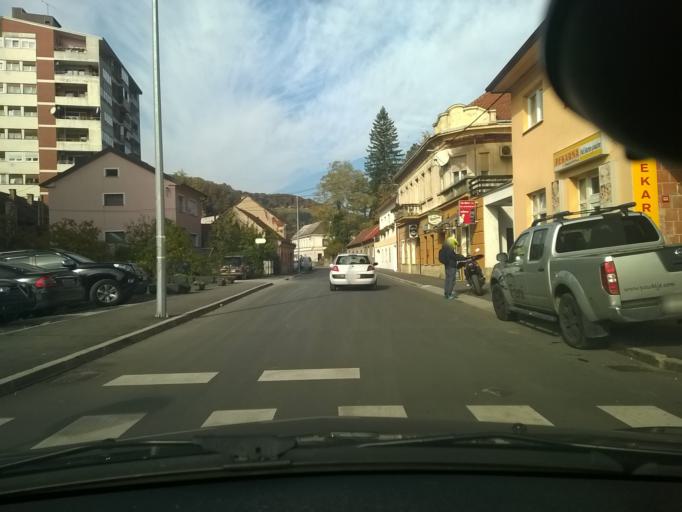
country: HR
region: Krapinsko-Zagorska
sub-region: Grad Krapina
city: Krapina
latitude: 46.1667
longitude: 15.8673
